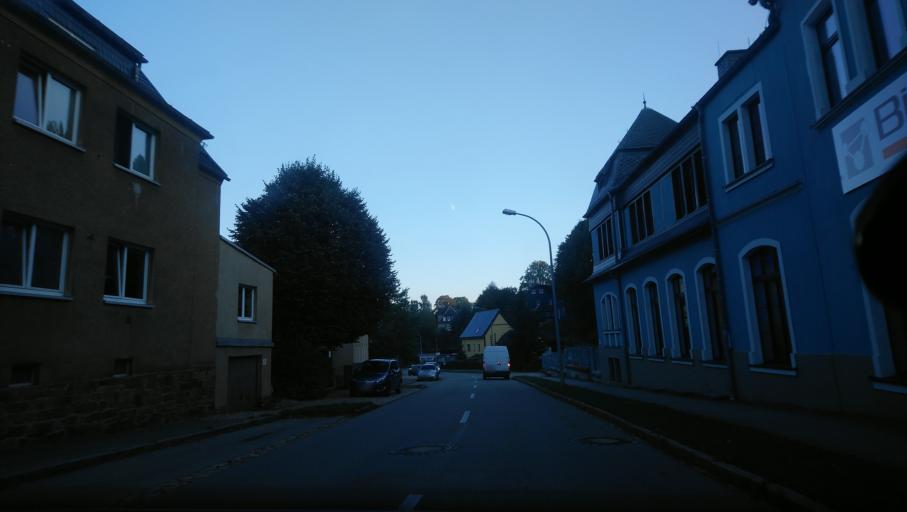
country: DE
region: Saxony
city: Geyer
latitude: 50.6186
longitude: 12.9260
